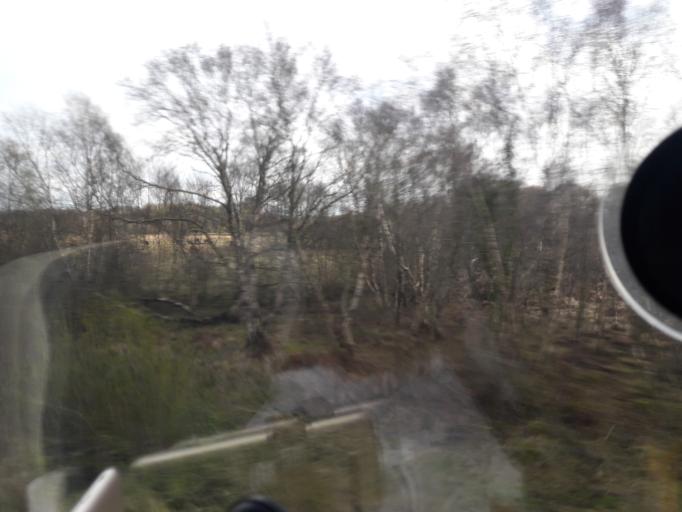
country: IE
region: Leinster
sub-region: An Iarmhi
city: Kinnegad
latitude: 53.4814
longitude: -7.0796
